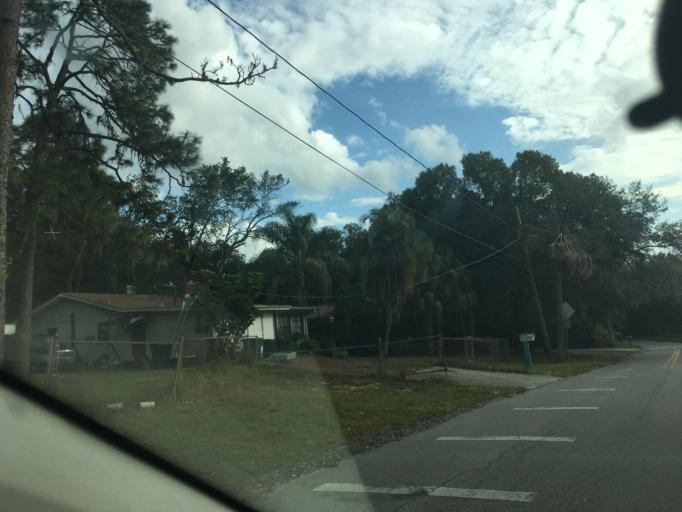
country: US
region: Florida
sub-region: Hillsborough County
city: Temple Terrace
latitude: 28.0229
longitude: -82.4182
